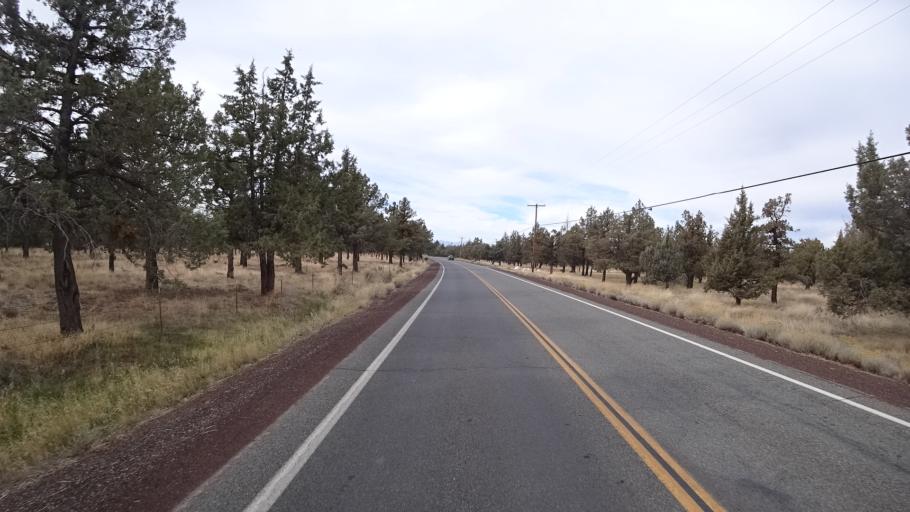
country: US
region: California
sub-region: Siskiyou County
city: Weed
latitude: 41.5923
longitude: -122.3081
